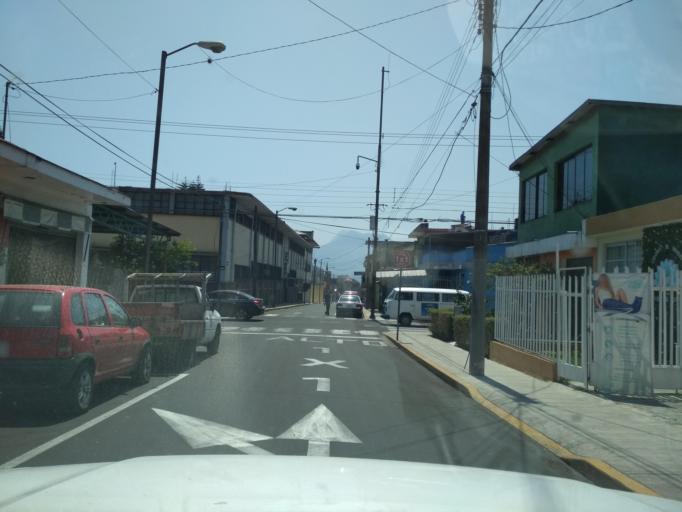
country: MX
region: Veracruz
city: Orizaba
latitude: 18.8517
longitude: -97.0904
